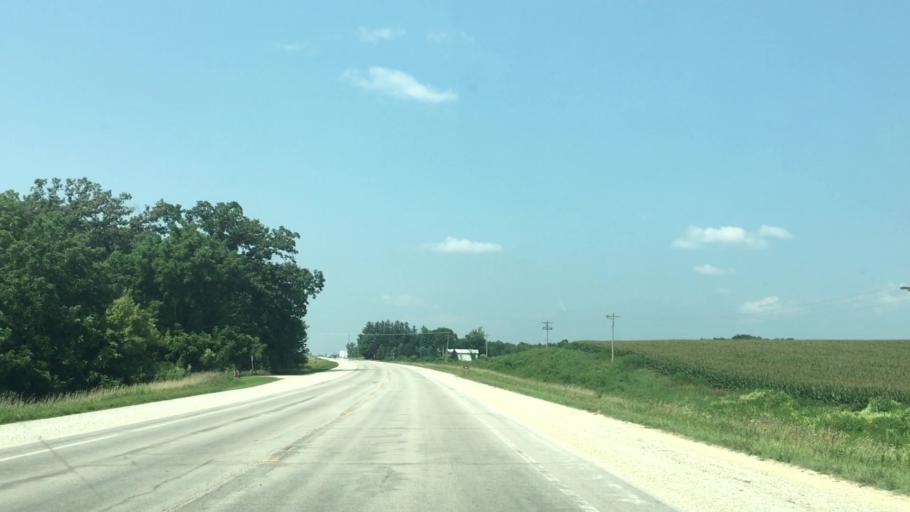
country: US
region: Iowa
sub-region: Winneshiek County
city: Decorah
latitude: 43.4258
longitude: -91.8592
